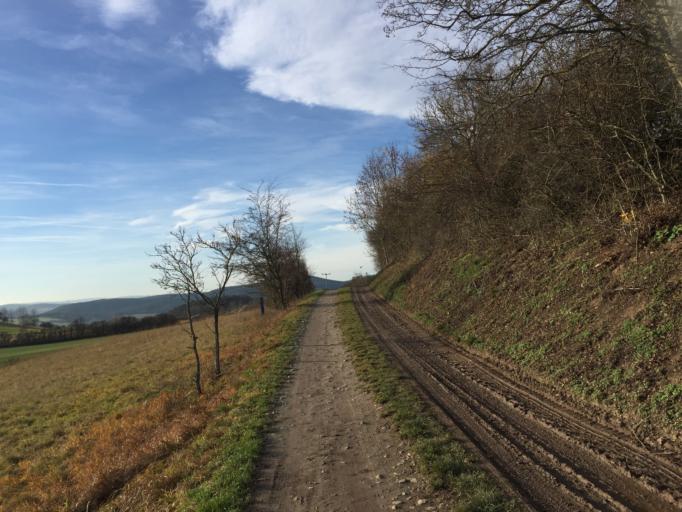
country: DE
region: Thuringia
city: Orlamunde
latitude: 50.7785
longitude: 11.5048
